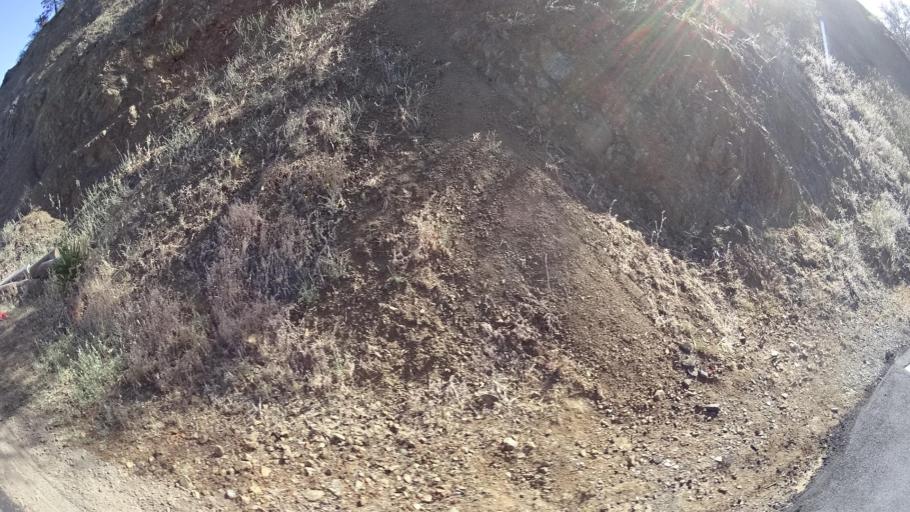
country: US
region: California
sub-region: Lake County
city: Clearlake
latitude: 38.9686
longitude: -122.6633
